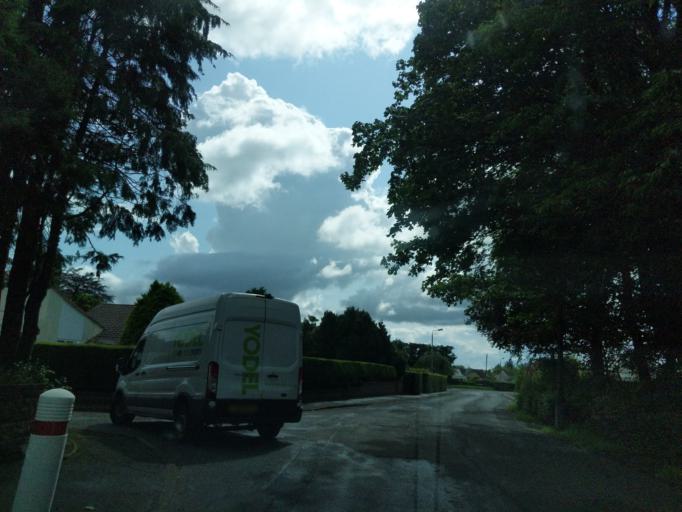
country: GB
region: Scotland
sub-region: East Ayrshire
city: Stewarton
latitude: 55.7130
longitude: -4.5292
